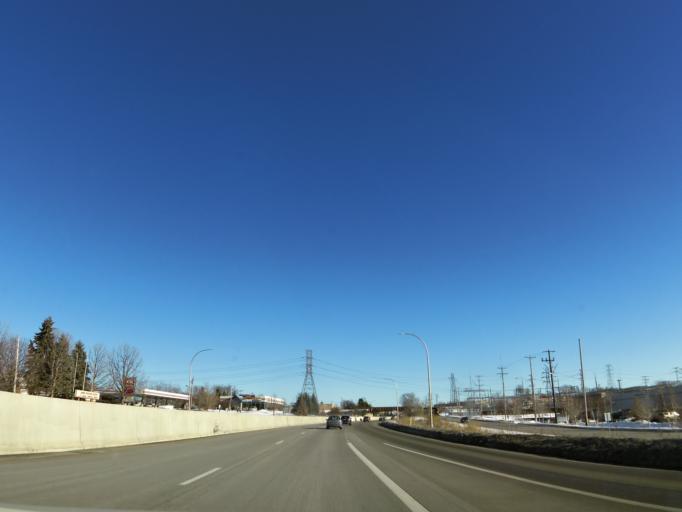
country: US
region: Minnesota
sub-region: Hennepin County
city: Saint Louis Park
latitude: 44.9382
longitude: -93.3667
